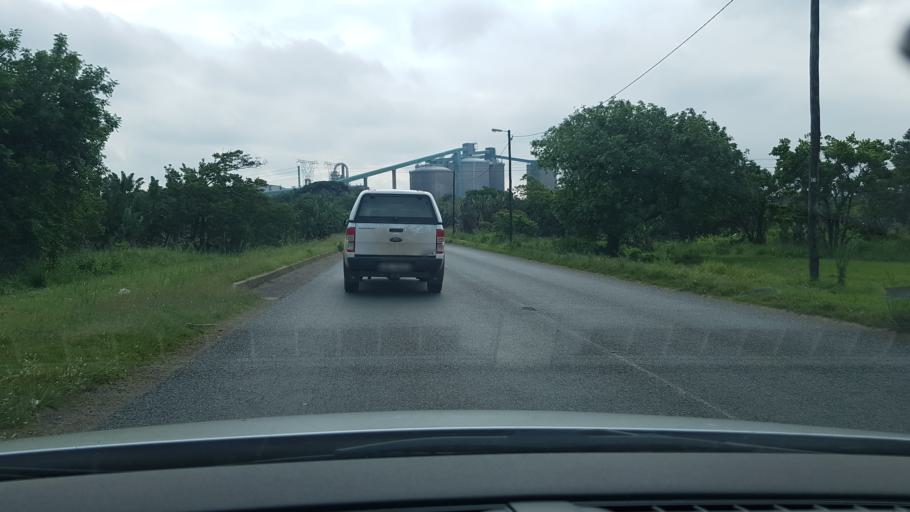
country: ZA
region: KwaZulu-Natal
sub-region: uThungulu District Municipality
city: Richards Bay
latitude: -28.7626
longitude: 32.0414
